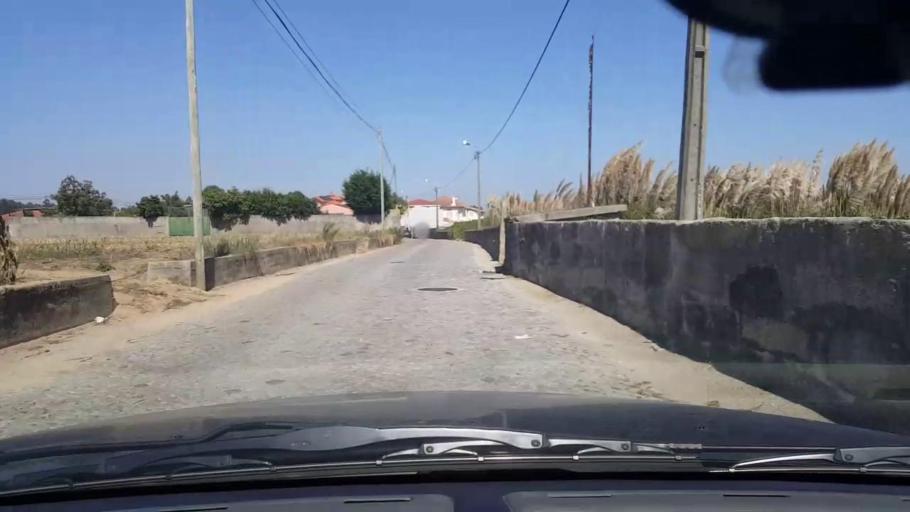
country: PT
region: Porto
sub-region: Matosinhos
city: Lavra
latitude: 41.2650
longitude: -8.6965
